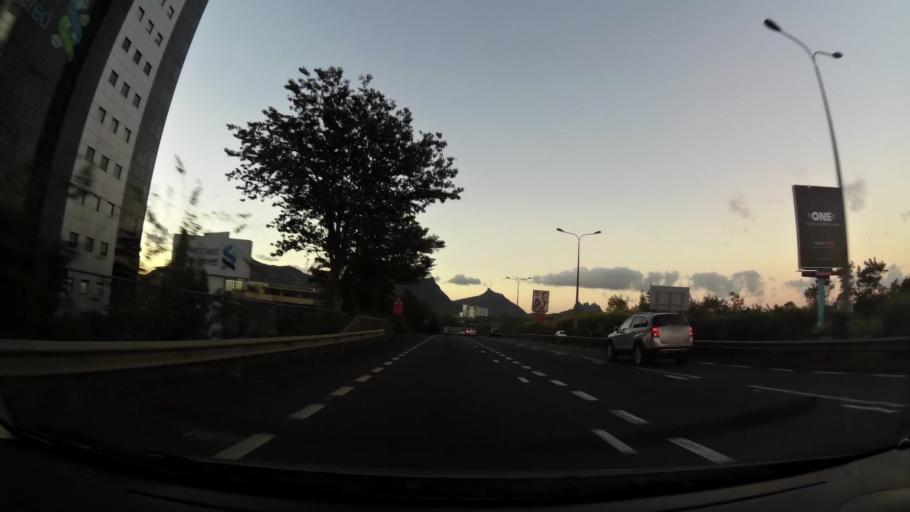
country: MU
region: Plaines Wilhems
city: Ebene
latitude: -20.2434
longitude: 57.4967
